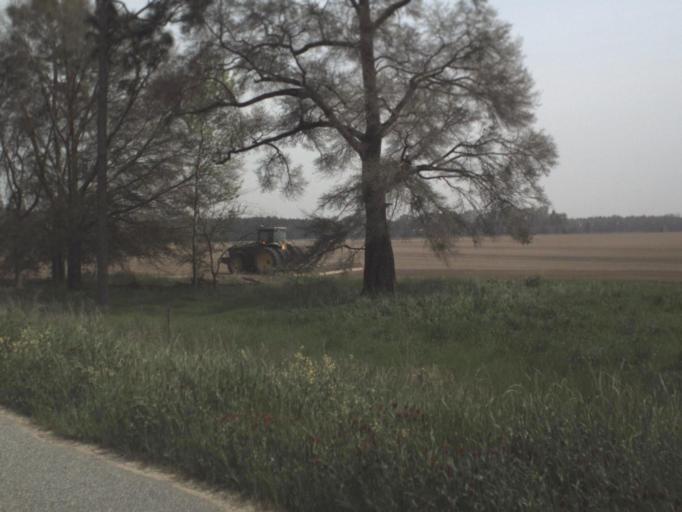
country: US
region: Florida
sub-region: Jackson County
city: Malone
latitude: 30.9757
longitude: -85.0555
